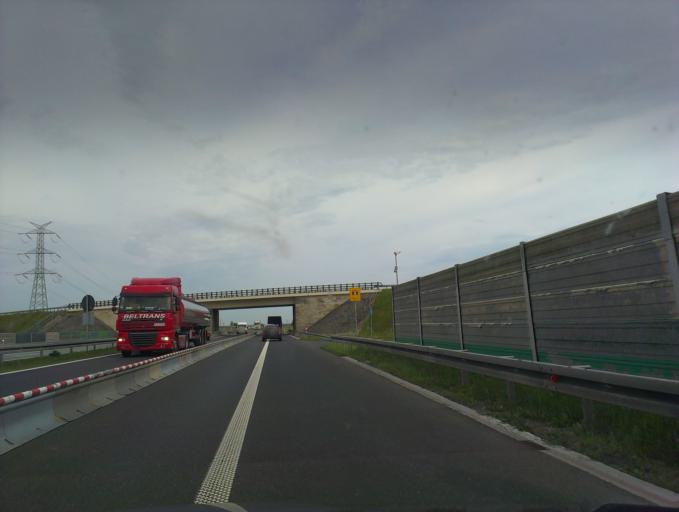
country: PL
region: Opole Voivodeship
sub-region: Powiat brzeski
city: Losiow
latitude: 50.7199
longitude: 17.5416
